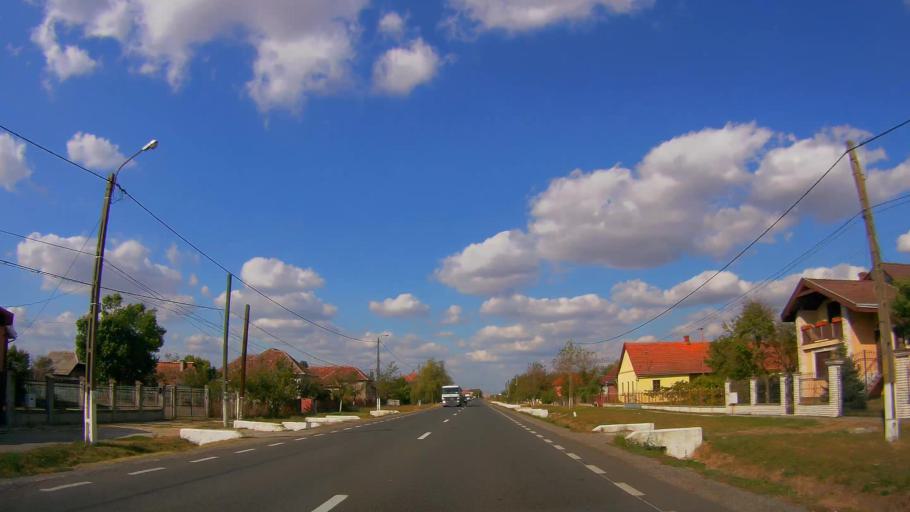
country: RO
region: Satu Mare
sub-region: Oras Ardud
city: Madaras
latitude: 47.6883
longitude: 22.8649
